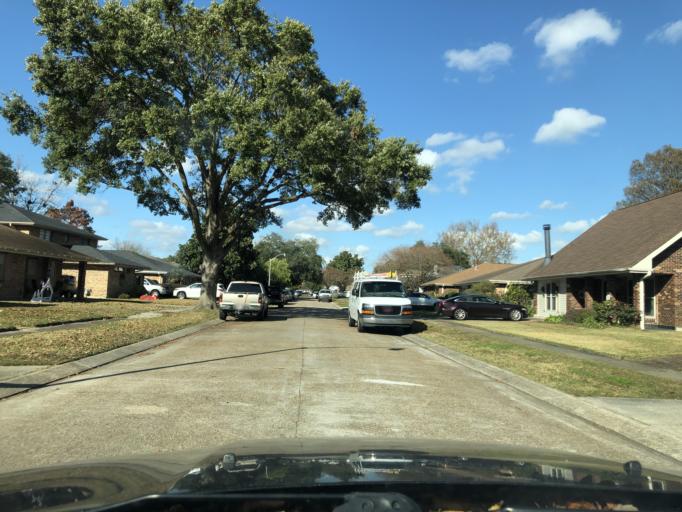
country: US
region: Louisiana
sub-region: Jefferson Parish
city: Metairie Terrace
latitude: 29.9885
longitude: -90.1653
